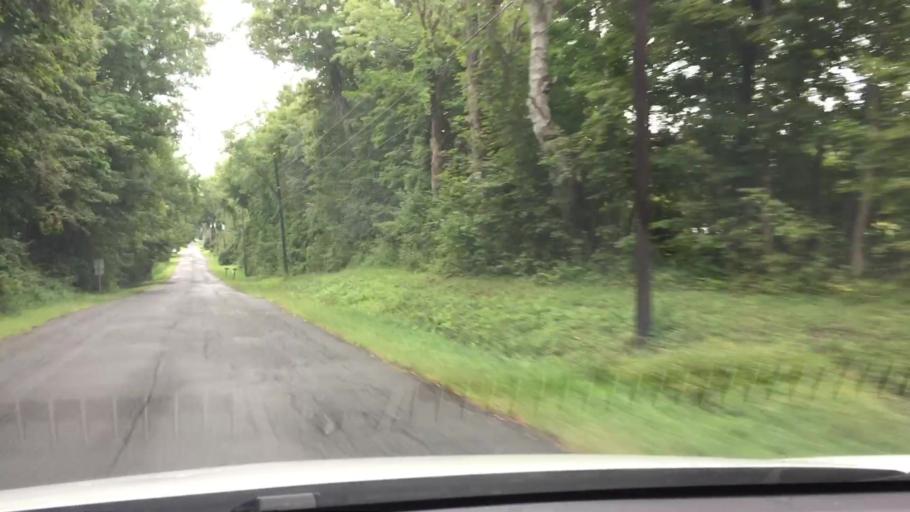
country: US
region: Massachusetts
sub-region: Berkshire County
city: Richmond
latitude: 42.4065
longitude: -73.3534
